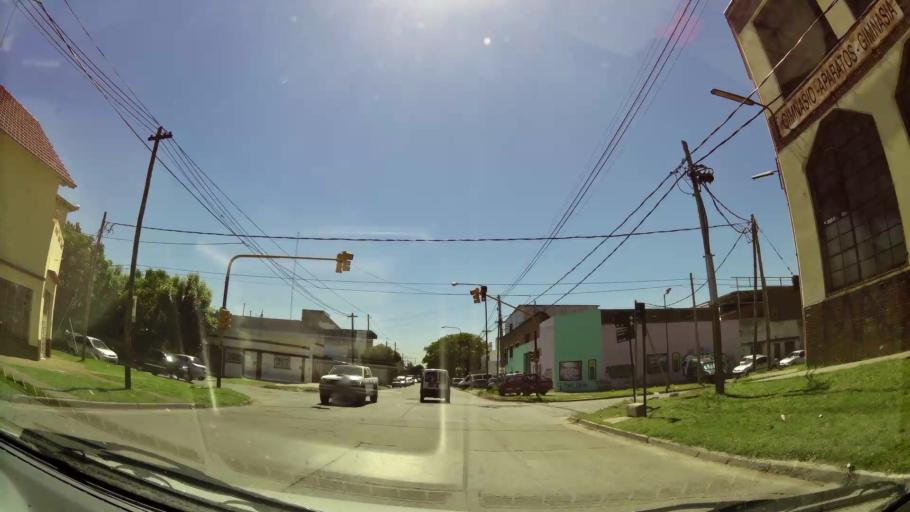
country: AR
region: Buenos Aires
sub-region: Partido de Quilmes
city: Quilmes
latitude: -34.7210
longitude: -58.2835
